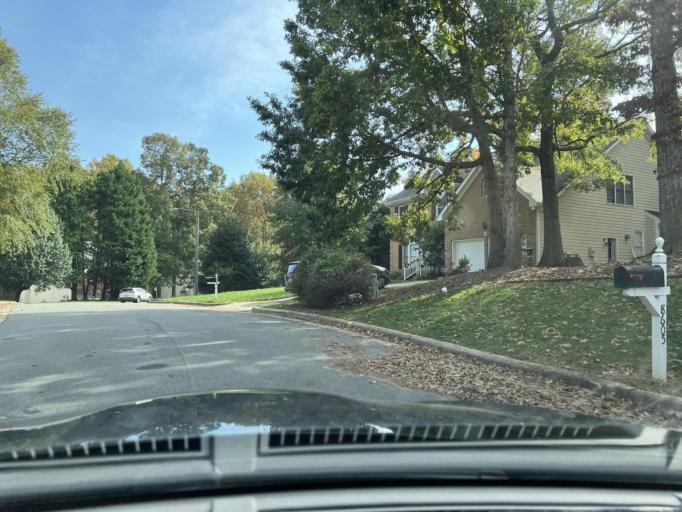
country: US
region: North Carolina
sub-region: Wake County
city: Wake Forest
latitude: 35.8959
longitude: -78.5834
